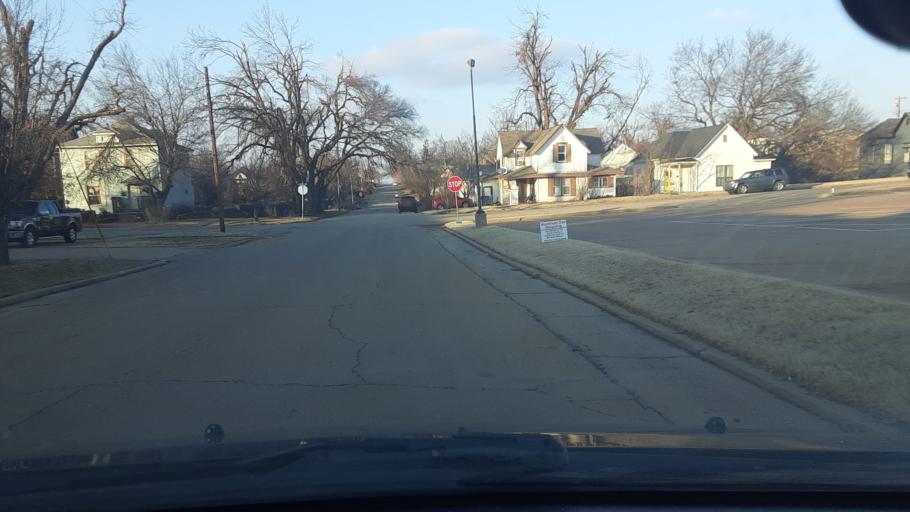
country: US
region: Oklahoma
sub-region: Logan County
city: Guthrie
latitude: 35.8807
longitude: -97.4215
